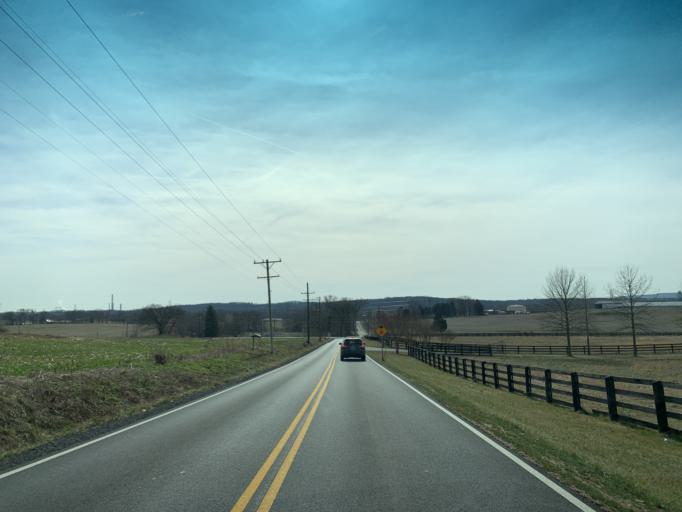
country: US
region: Maryland
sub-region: Frederick County
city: Adamstown
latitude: 39.2621
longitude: -77.4765
